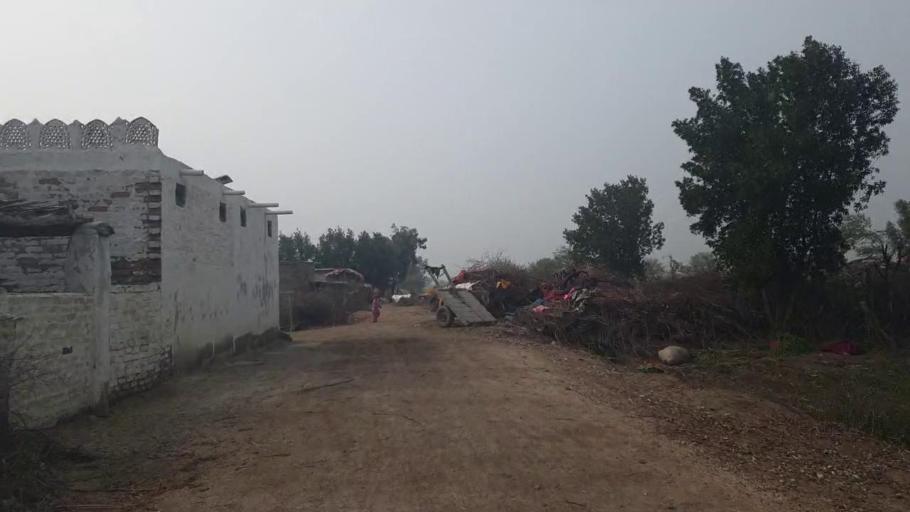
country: PK
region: Sindh
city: Tando Adam
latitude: 25.7577
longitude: 68.7007
